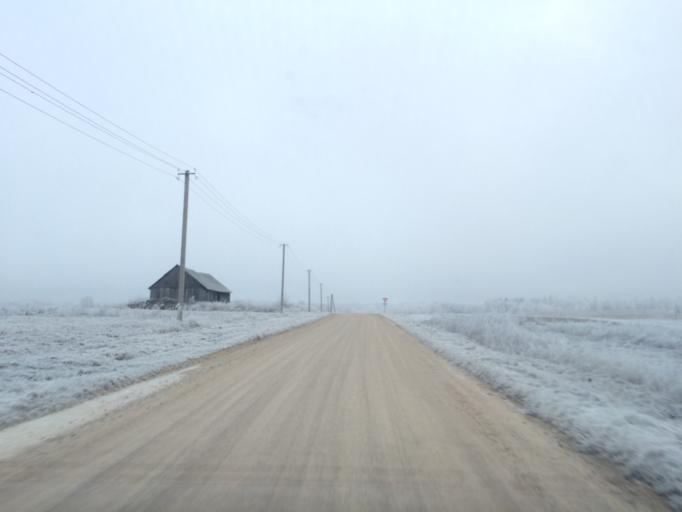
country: LV
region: Ludzas Rajons
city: Ludza
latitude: 56.6180
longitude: 27.5183
